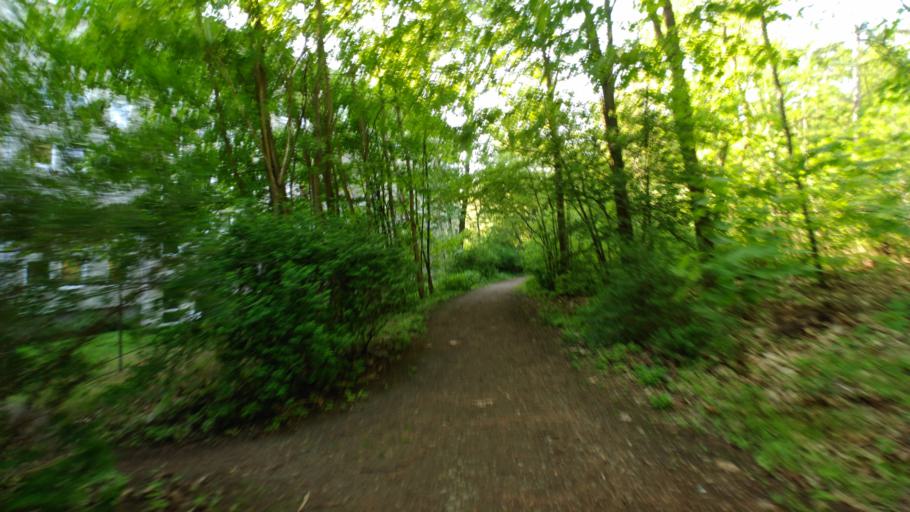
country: DE
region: Saxony
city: Albertstadt
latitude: 51.0752
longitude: 13.7917
